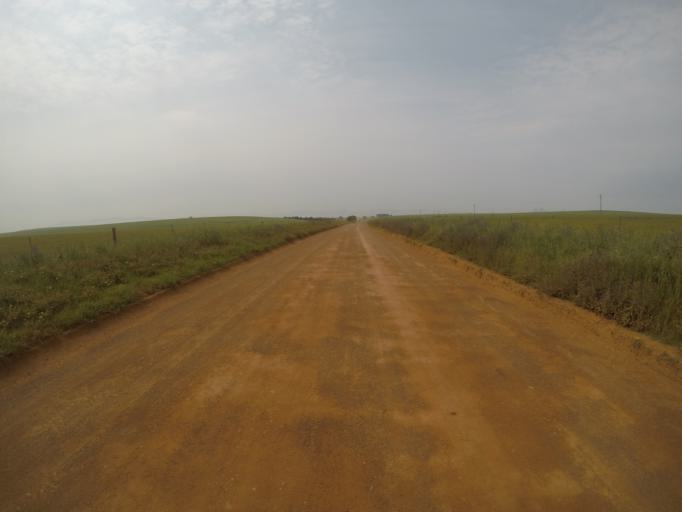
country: ZA
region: Western Cape
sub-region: City of Cape Town
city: Kraaifontein
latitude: -33.7258
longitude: 18.6463
